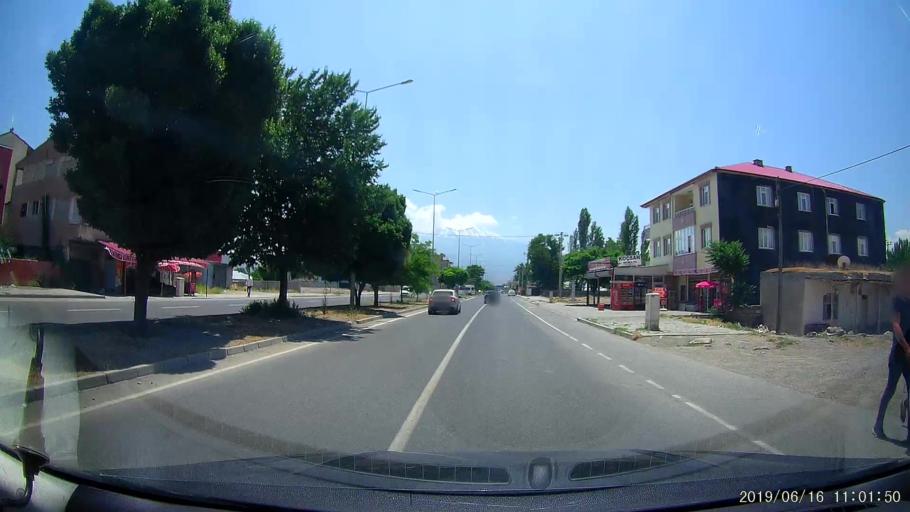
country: TR
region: Igdir
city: Igdir
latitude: 39.9121
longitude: 44.0540
